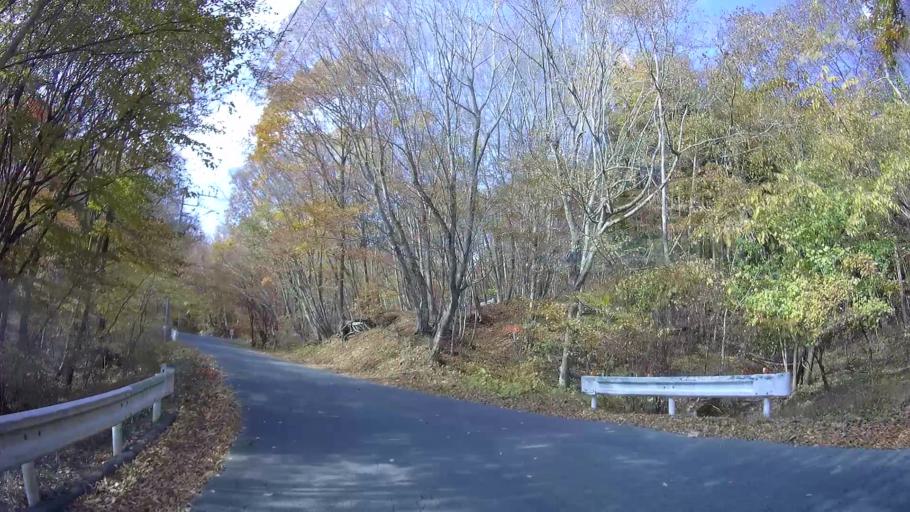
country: JP
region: Gunma
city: Nakanojomachi
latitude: 36.5174
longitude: 138.6671
